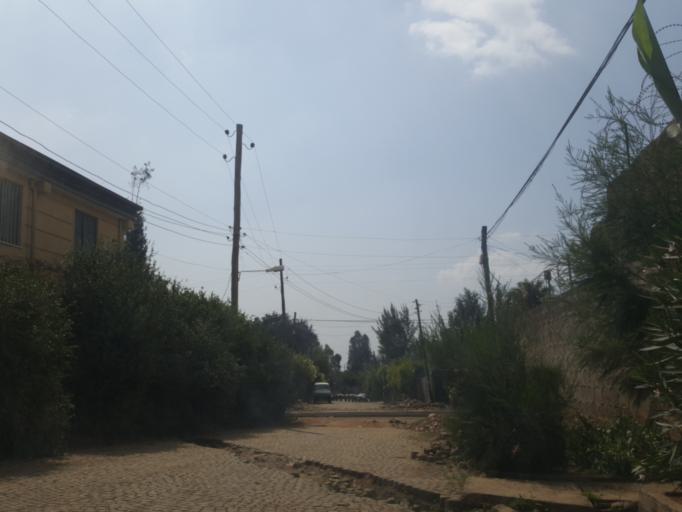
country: ET
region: Adis Abeba
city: Addis Ababa
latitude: 9.0586
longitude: 38.7207
